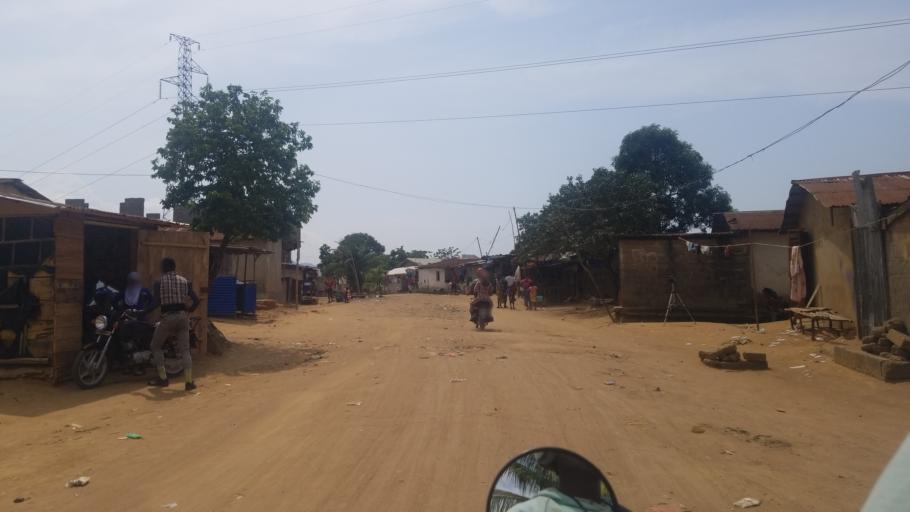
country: SL
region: Western Area
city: Waterloo
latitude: 8.3256
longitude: -13.0480
